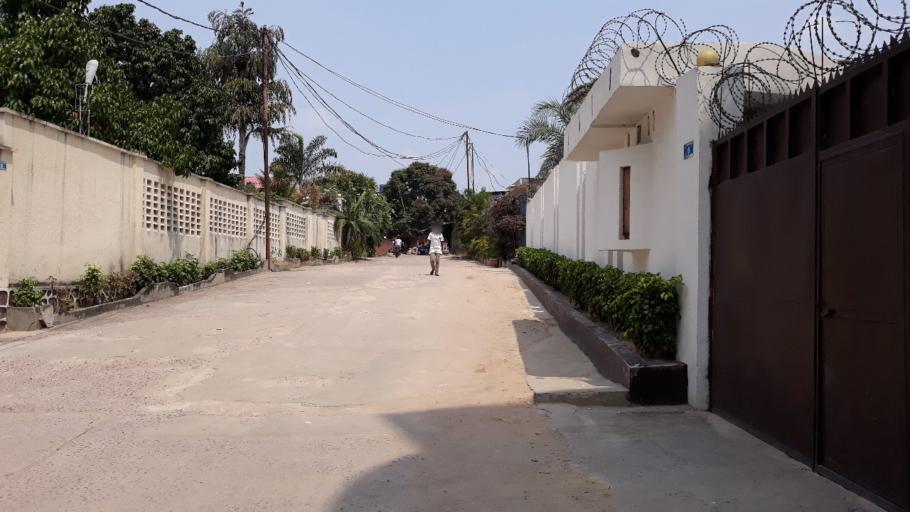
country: CD
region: Kinshasa
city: Kinshasa
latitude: -4.3265
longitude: 15.2770
